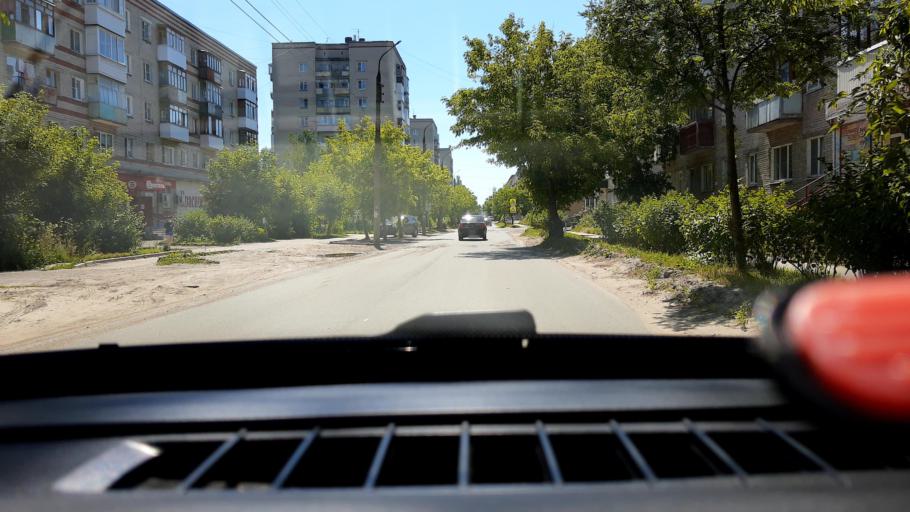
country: RU
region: Nizjnij Novgorod
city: Dzerzhinsk
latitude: 56.2539
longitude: 43.4746
